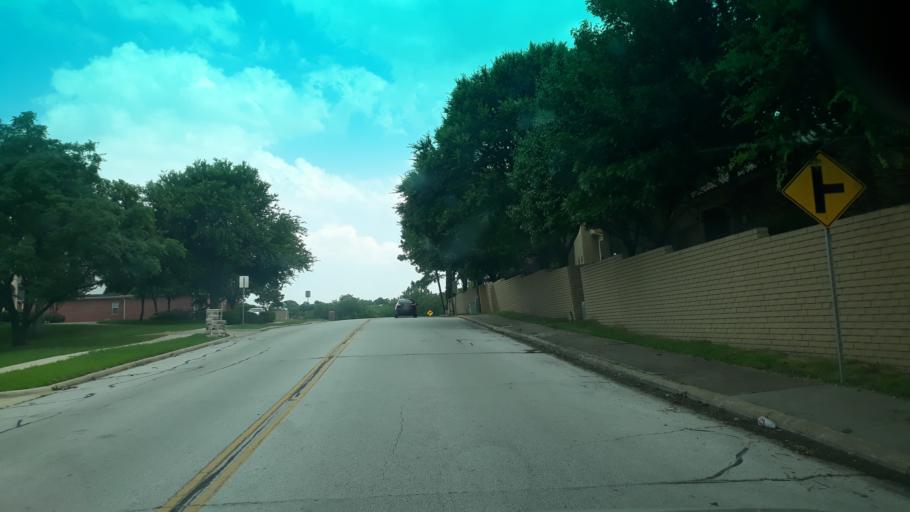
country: US
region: Texas
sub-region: Dallas County
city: Irving
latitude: 32.8616
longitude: -96.9802
